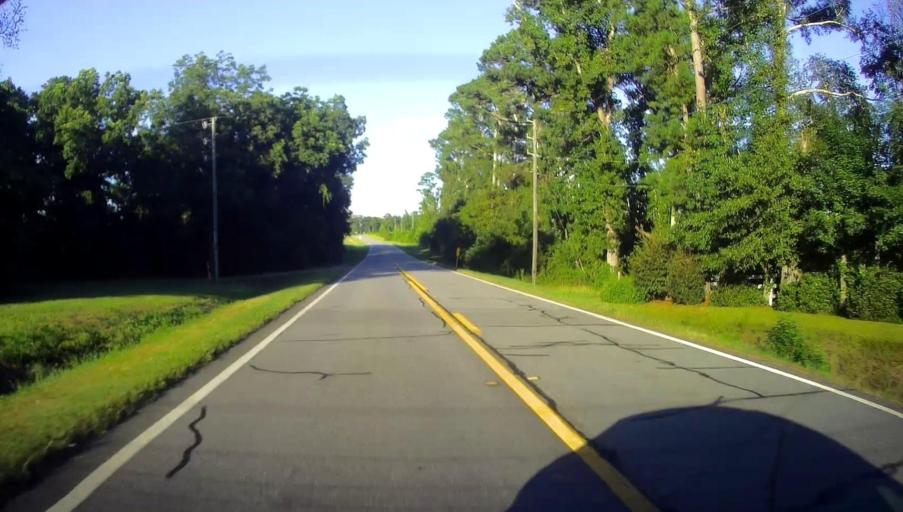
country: US
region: Georgia
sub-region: Pulaski County
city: Hawkinsville
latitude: 32.2683
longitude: -83.5110
